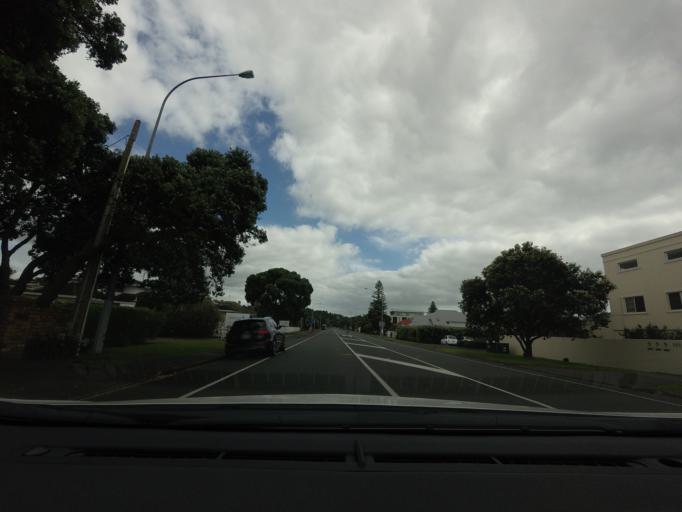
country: NZ
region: Auckland
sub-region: Auckland
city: Rothesay Bay
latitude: -36.5831
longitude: 174.6937
